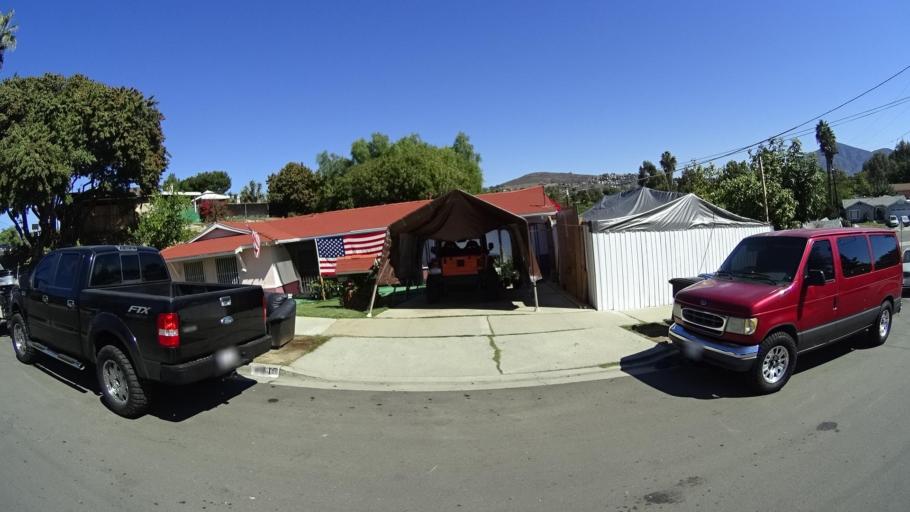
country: US
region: California
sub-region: San Diego County
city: La Presa
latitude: 32.7157
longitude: -117.0182
